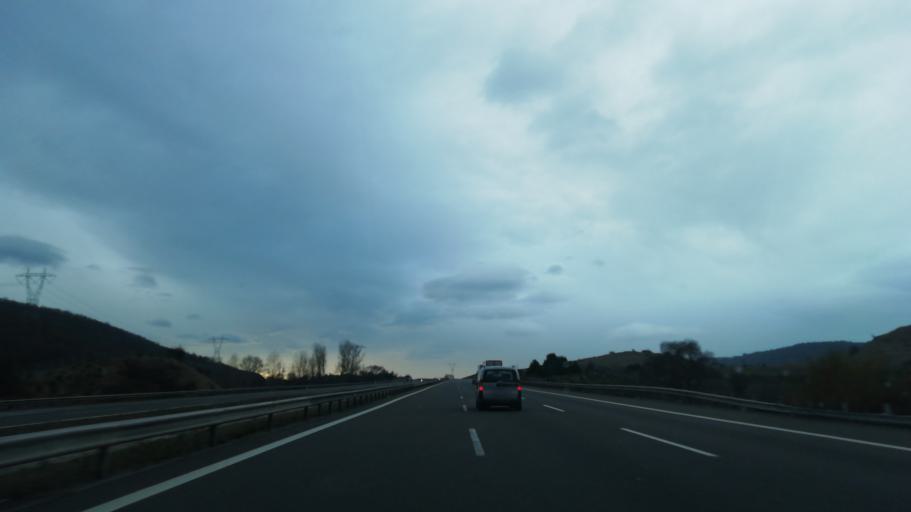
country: TR
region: Bolu
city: Yenicaga
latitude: 40.7620
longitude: 31.9892
